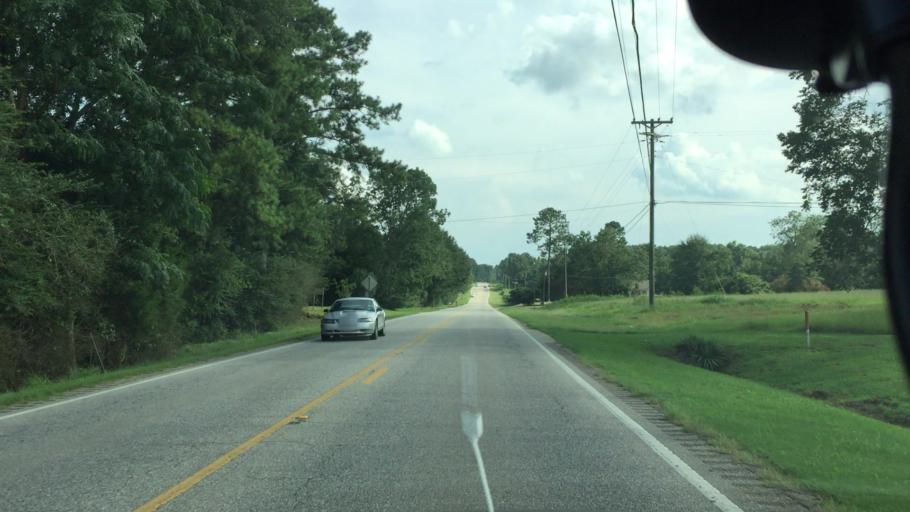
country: US
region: Alabama
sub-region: Pike County
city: Troy
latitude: 31.7366
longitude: -85.9572
